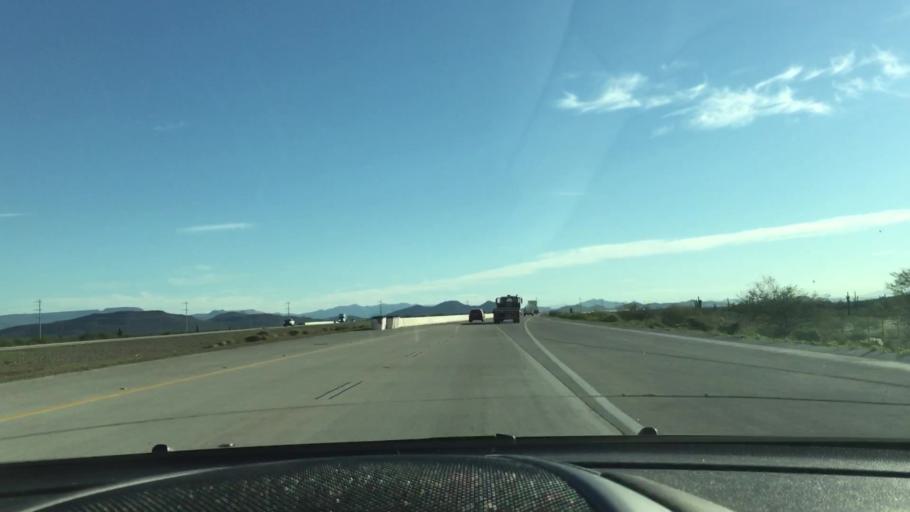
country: US
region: Arizona
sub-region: Maricopa County
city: Anthem
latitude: 33.7797
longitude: -112.2115
